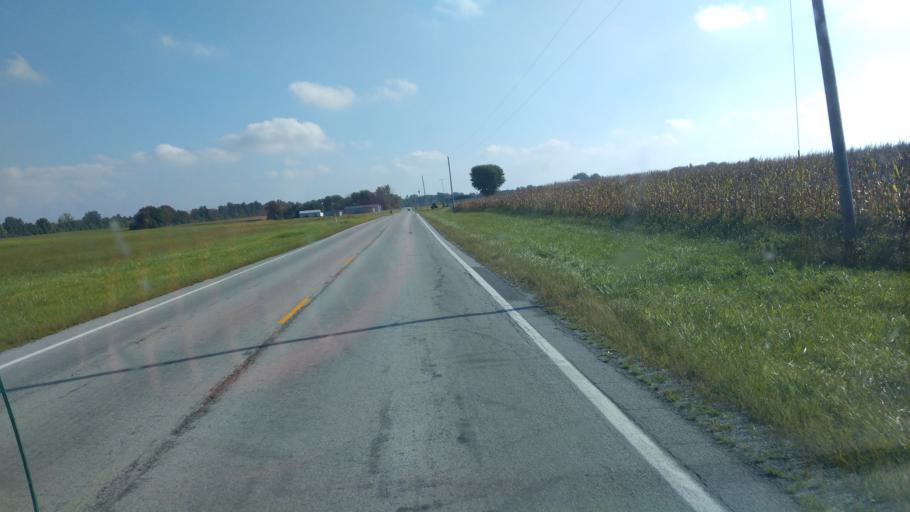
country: US
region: Ohio
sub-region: Hardin County
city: Forest
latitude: 40.8161
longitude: -83.5200
